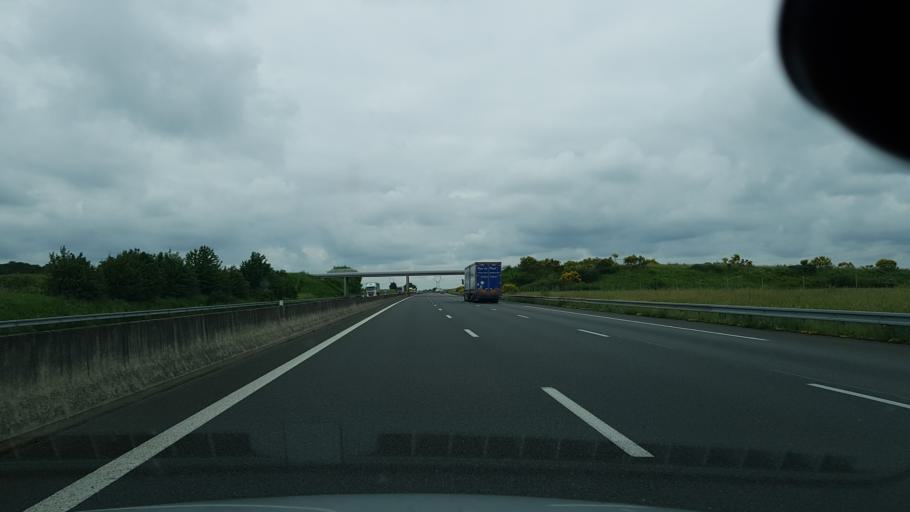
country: FR
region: Centre
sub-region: Departement du Loir-et-Cher
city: Herbault
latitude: 47.6163
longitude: 1.1977
